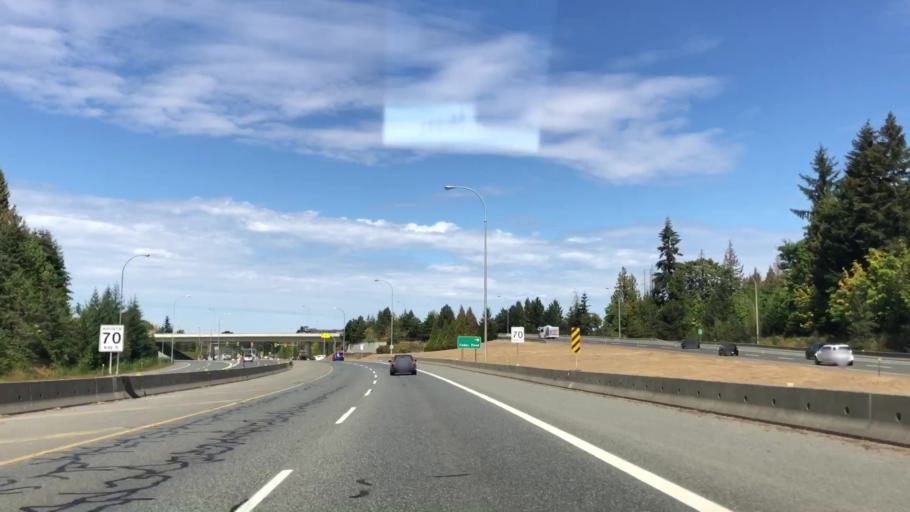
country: CA
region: British Columbia
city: Nanaimo
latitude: 49.1218
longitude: -123.9143
